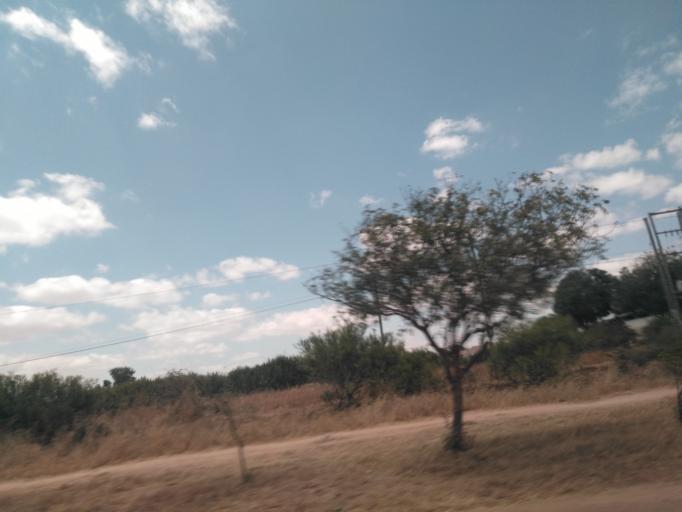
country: TZ
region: Dodoma
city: Kisasa
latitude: -6.1616
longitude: 35.7923
